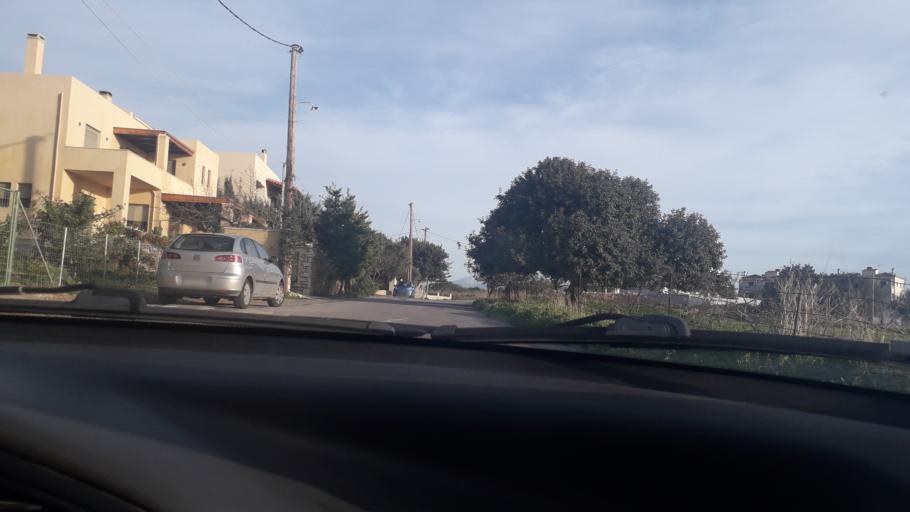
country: GR
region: Crete
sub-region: Nomos Rethymnis
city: Panormos
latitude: 35.3890
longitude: 24.6141
